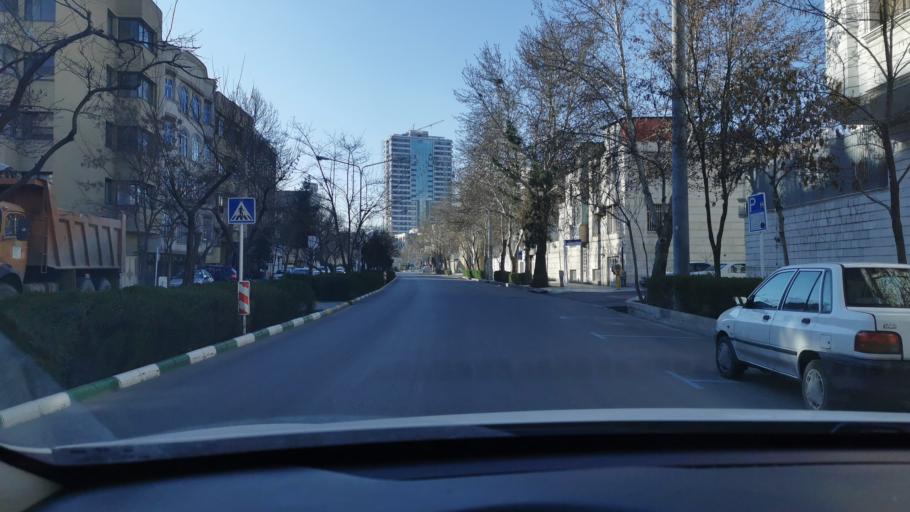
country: IR
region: Razavi Khorasan
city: Mashhad
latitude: 36.2881
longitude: 59.5673
